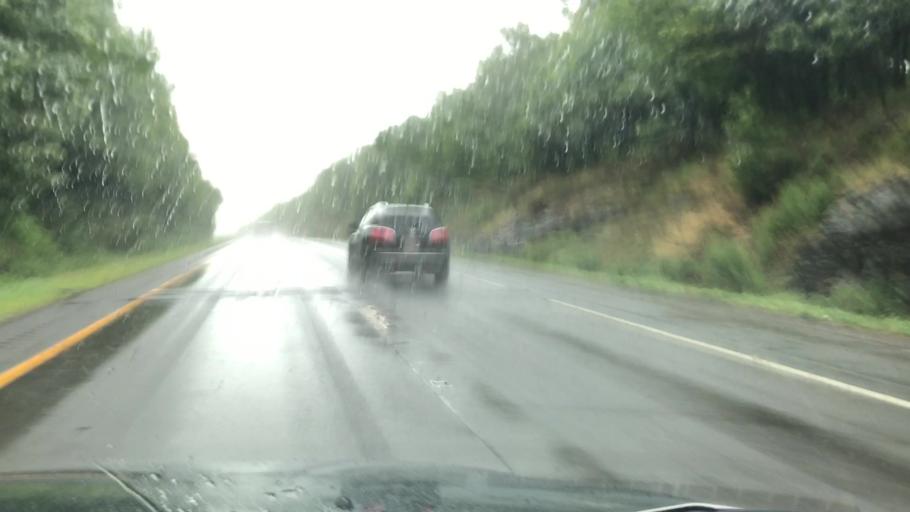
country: US
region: Pennsylvania
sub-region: Pike County
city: Gold Key Lake
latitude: 41.3496
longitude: -74.9442
